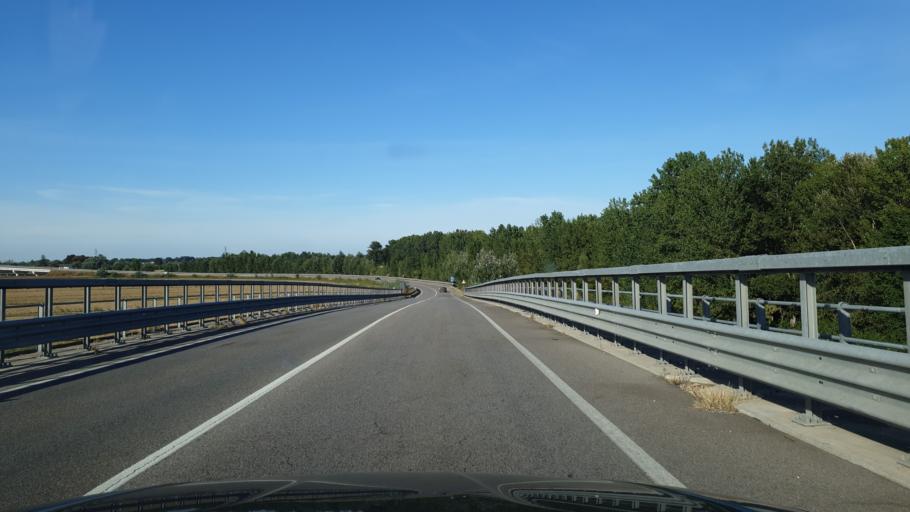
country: IT
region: Emilia-Romagna
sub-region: Provincia di Ravenna
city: Alfonsine
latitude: 44.4992
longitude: 12.0590
